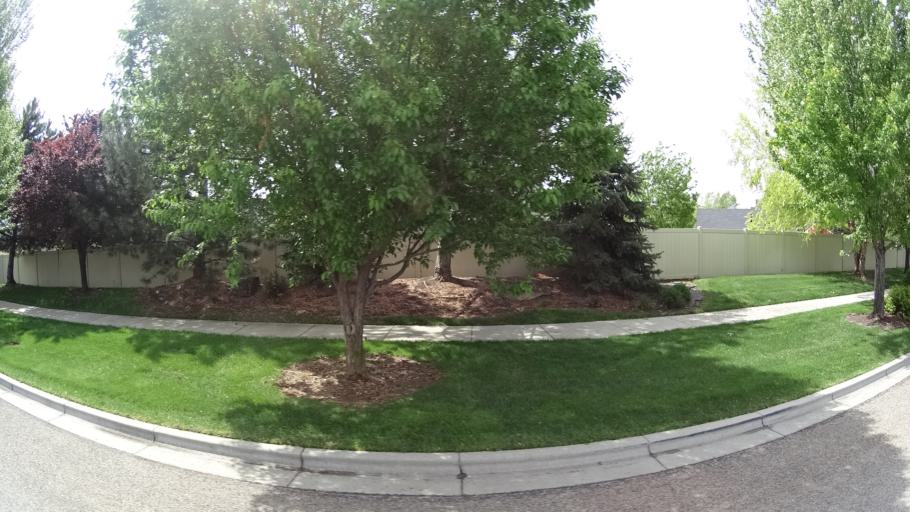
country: US
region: Idaho
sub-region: Ada County
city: Meridian
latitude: 43.5538
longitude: -116.3236
